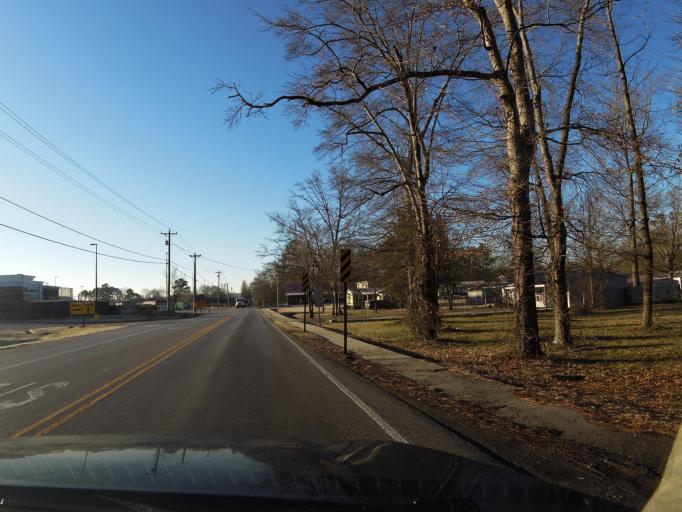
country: US
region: Alabama
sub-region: Morgan County
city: Falkville
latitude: 34.3681
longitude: -86.8945
